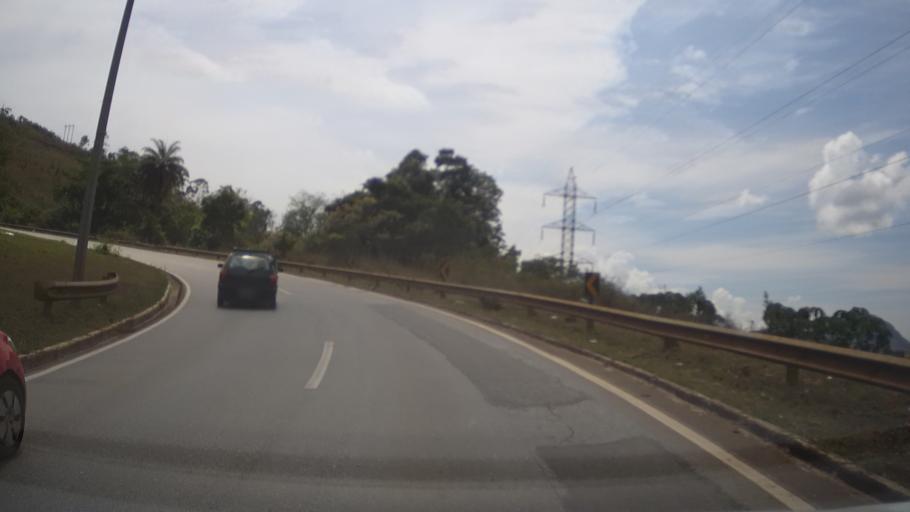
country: BR
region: Minas Gerais
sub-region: Nova Lima
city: Nova Lima
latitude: -19.9968
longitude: -43.9153
